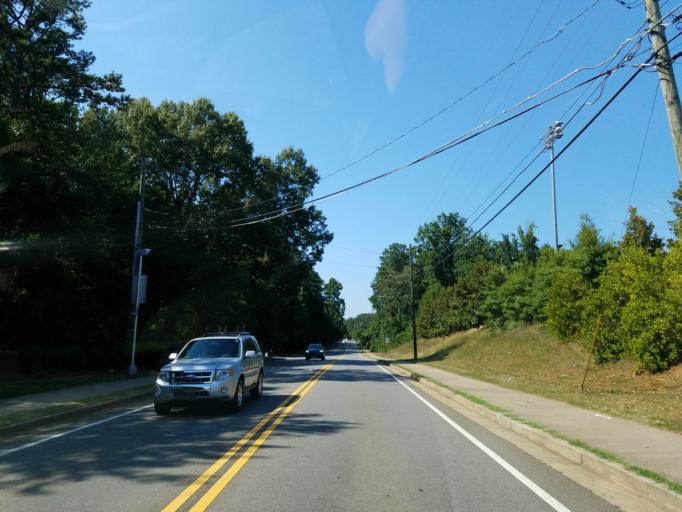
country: US
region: Georgia
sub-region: Fulton County
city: Milton
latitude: 34.0991
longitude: -84.3393
